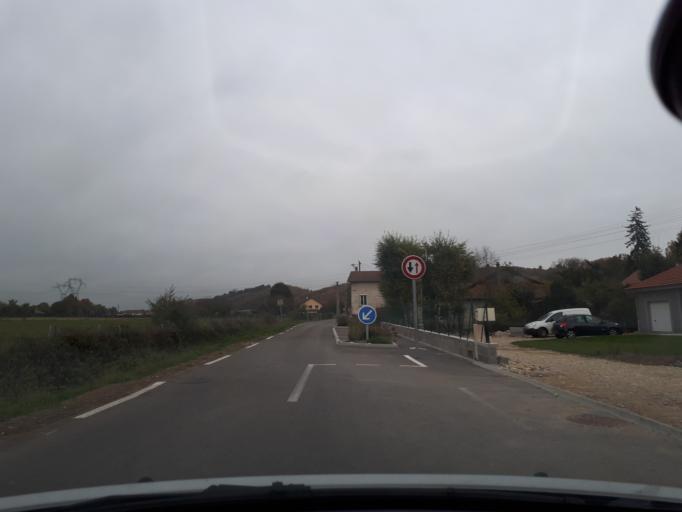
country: FR
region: Rhone-Alpes
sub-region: Departement de l'Isere
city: Champier
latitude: 45.4599
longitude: 5.2951
